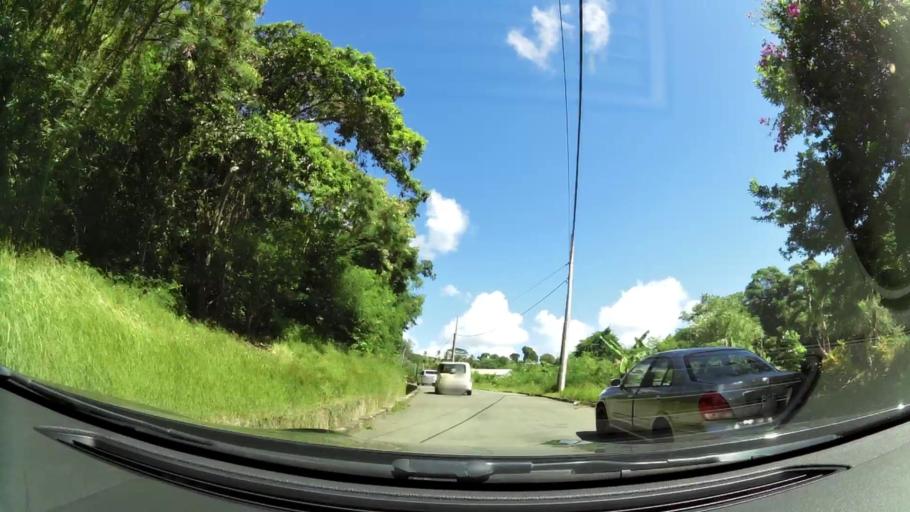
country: TT
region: Tobago
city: Scarborough
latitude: 11.1771
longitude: -60.7844
